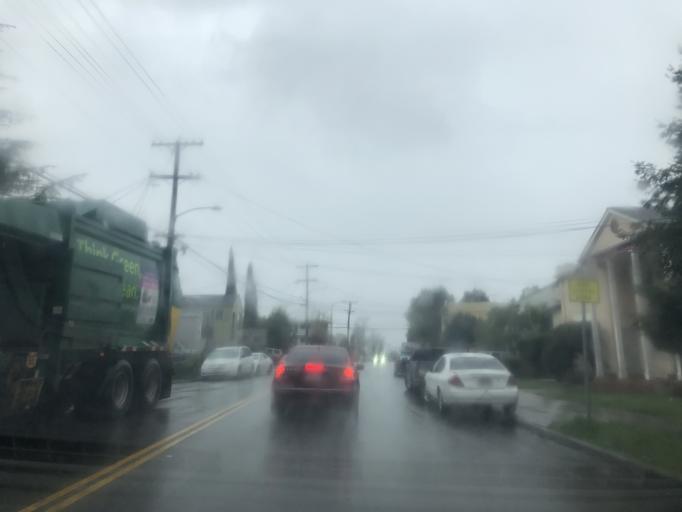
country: US
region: California
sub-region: Alameda County
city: San Leandro
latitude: 37.7745
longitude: -122.1806
